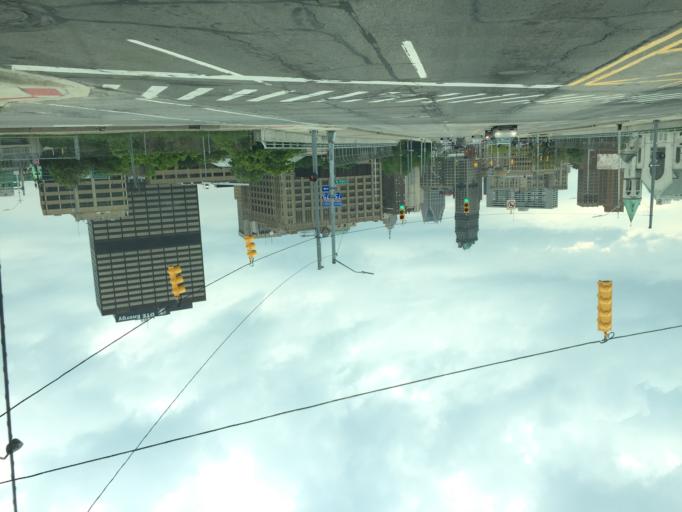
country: US
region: Michigan
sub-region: Wayne County
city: Detroit
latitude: 42.3369
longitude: -83.0603
